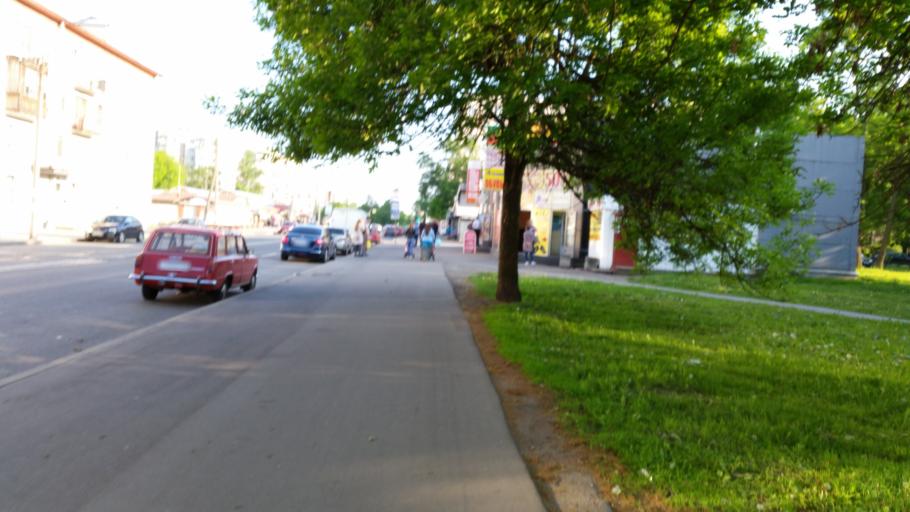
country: RU
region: St.-Petersburg
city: Sosnovaya Polyana
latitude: 59.8374
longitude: 30.1465
